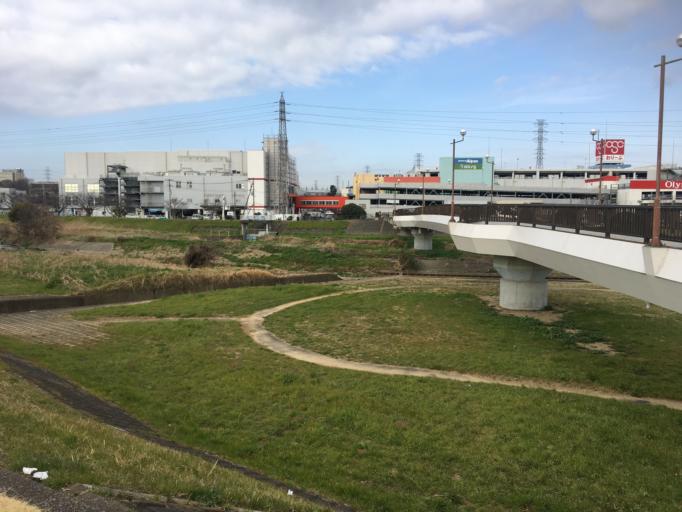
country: JP
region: Saitama
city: Shiki
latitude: 35.8168
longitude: 139.5518
